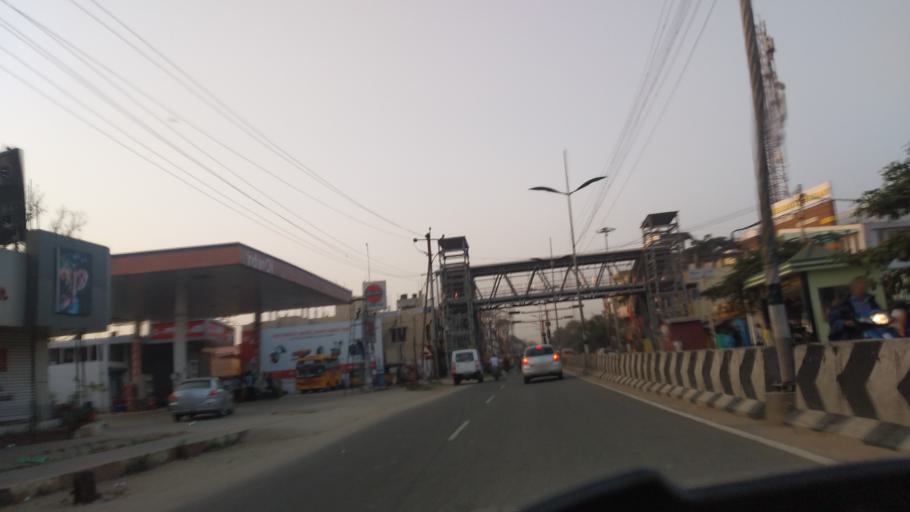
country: IN
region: Tamil Nadu
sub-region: Coimbatore
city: Perur
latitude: 10.9633
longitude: 76.9551
